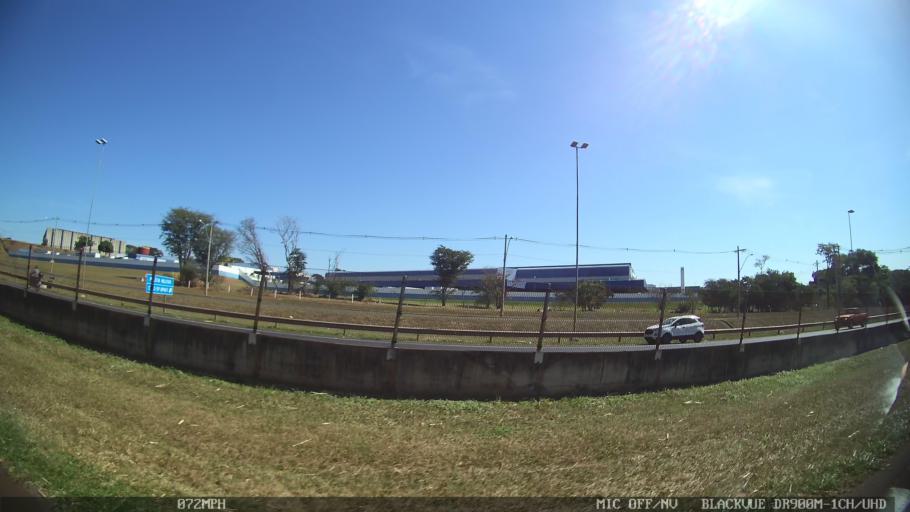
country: BR
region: Sao Paulo
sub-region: Ribeirao Preto
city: Ribeirao Preto
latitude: -21.2003
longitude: -47.7582
